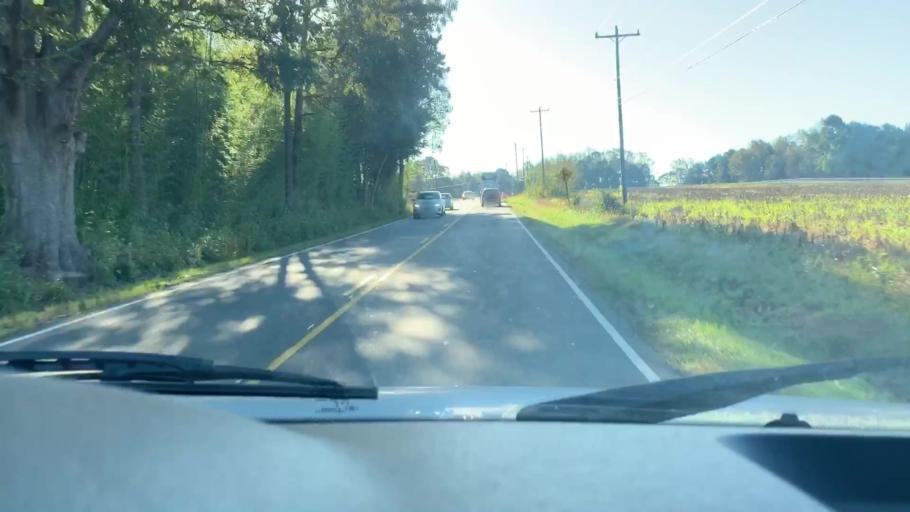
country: US
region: North Carolina
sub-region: Mecklenburg County
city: Huntersville
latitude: 35.4519
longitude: -80.7983
